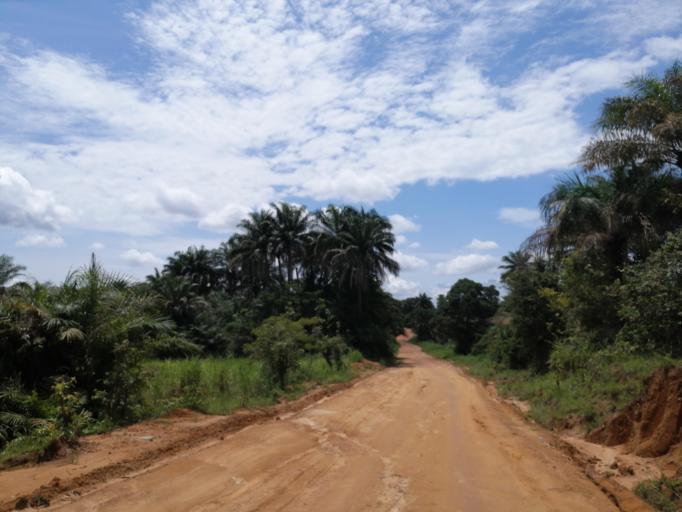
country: SL
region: Northern Province
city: Konakridee
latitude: 8.7498
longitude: -13.1446
